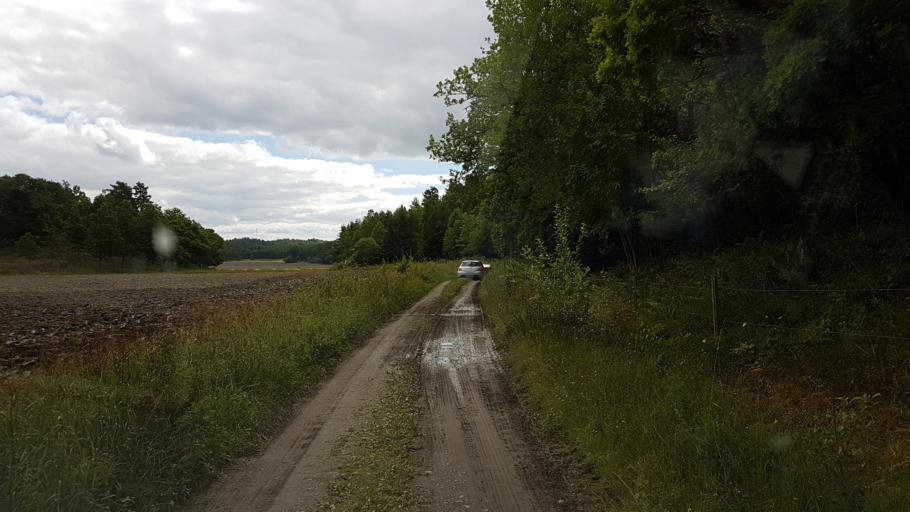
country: SE
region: OEstergoetland
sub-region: Valdemarsviks Kommun
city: Gusum
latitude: 58.4298
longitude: 16.5754
